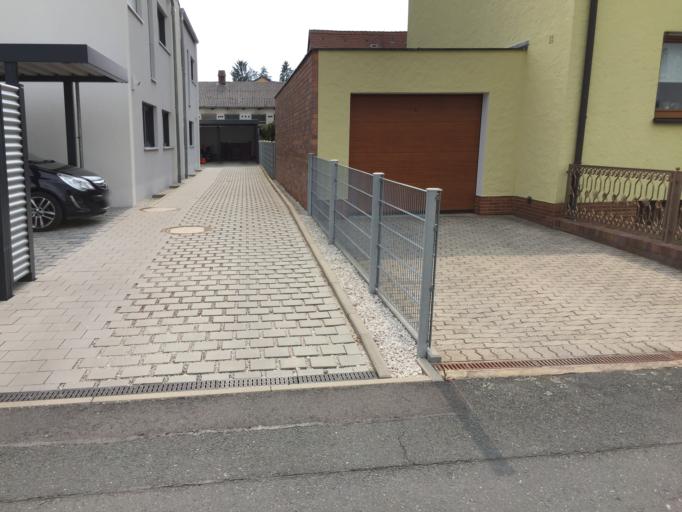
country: DE
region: Bavaria
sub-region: Regierungsbezirk Mittelfranken
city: Erlangen
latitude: 49.5675
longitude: 10.9652
